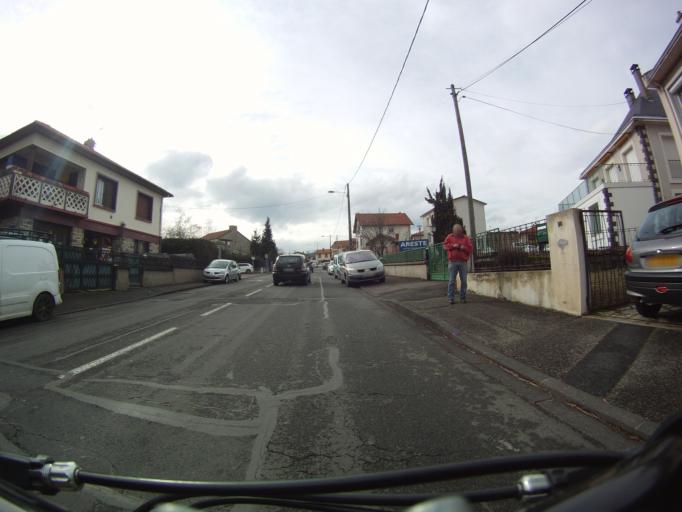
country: FR
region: Auvergne
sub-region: Departement du Puy-de-Dome
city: Aubiere
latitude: 45.7478
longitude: 3.1098
